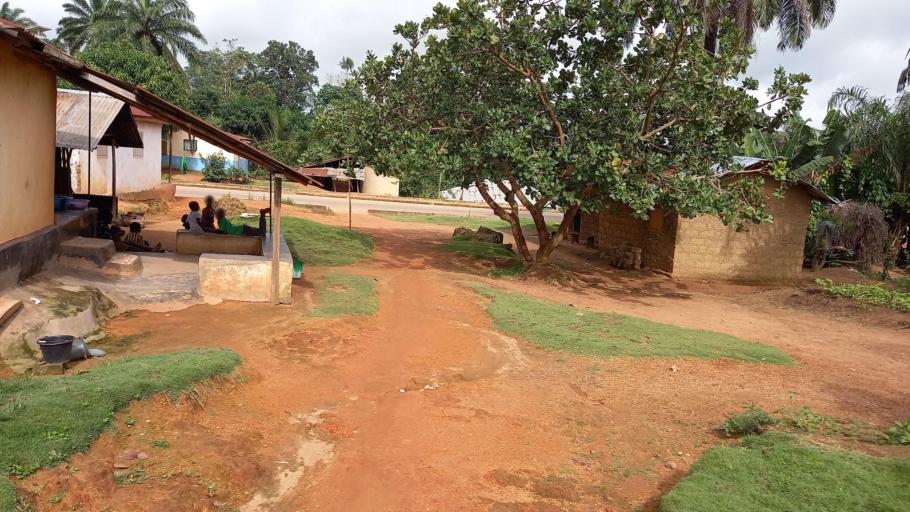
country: SL
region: Eastern Province
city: Kailahun
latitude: 8.2874
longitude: -10.5730
